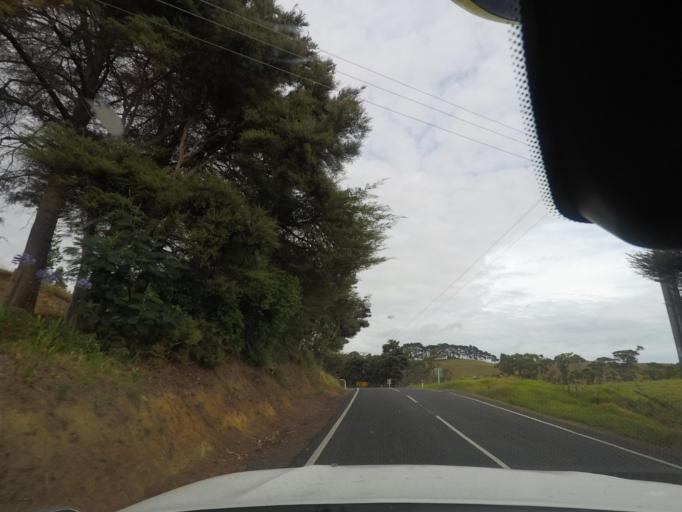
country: NZ
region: Auckland
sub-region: Auckland
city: Parakai
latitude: -36.5240
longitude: 174.2874
